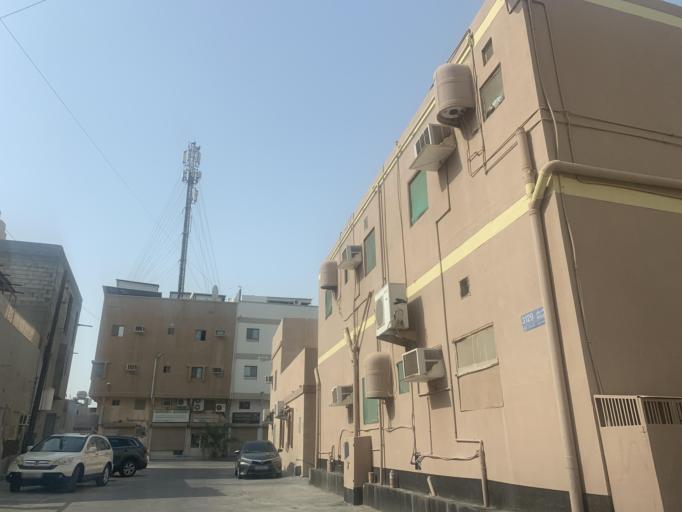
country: BH
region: Manama
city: Jidd Hafs
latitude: 26.2105
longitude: 50.4745
